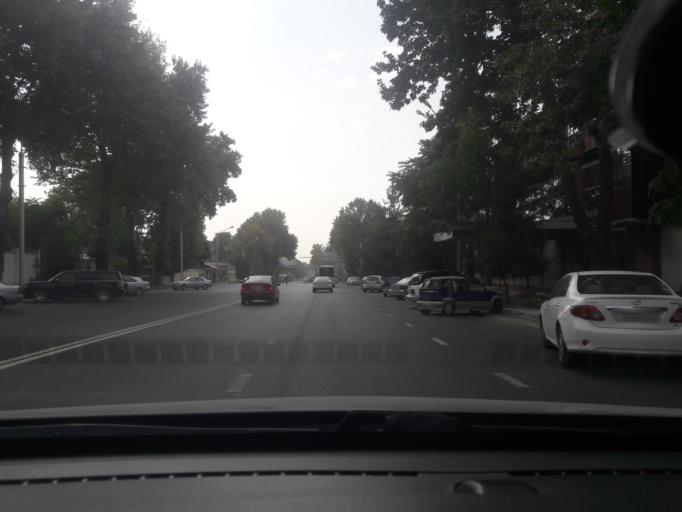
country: TJ
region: Dushanbe
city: Dushanbe
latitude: 38.5768
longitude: 68.8033
